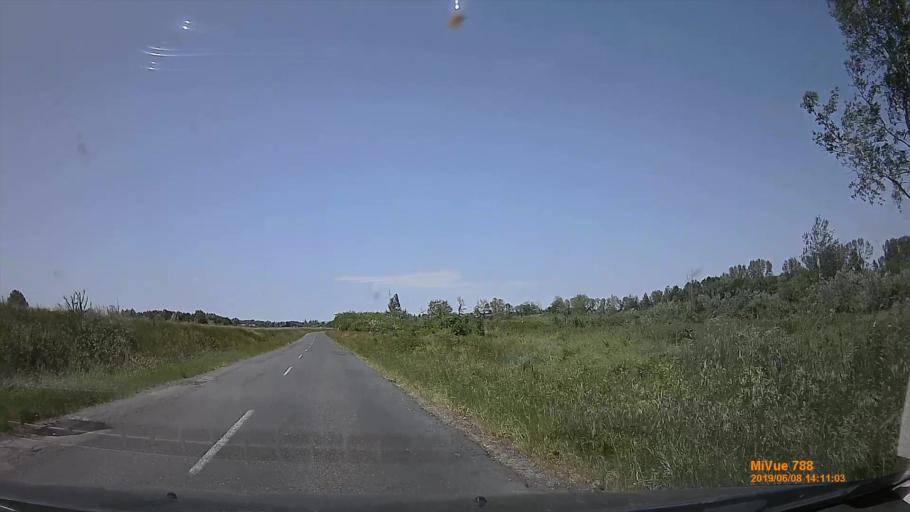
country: HU
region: Vas
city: Csepreg
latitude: 47.3807
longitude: 16.7166
